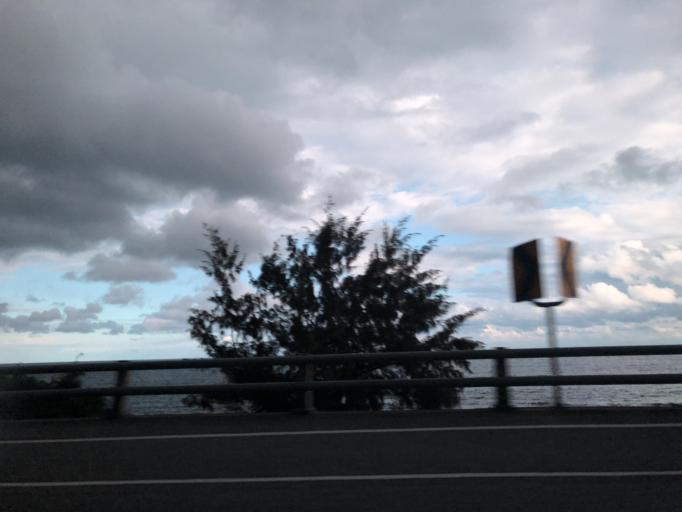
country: TW
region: Taiwan
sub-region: Taitung
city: Taitung
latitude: 22.8567
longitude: 121.1982
